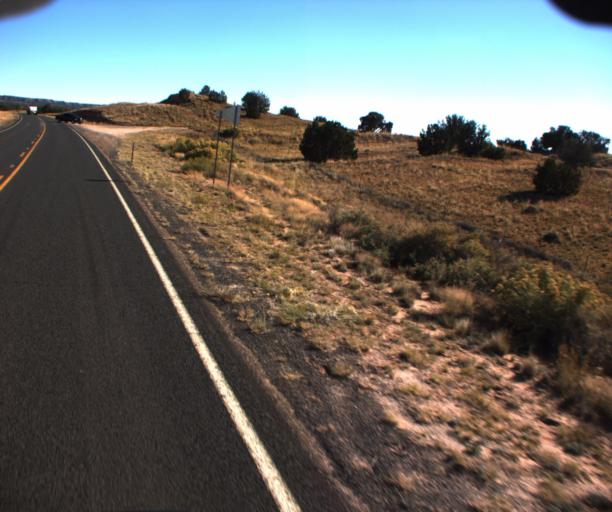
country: US
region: Arizona
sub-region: Apache County
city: Houck
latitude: 35.3836
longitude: -109.4961
